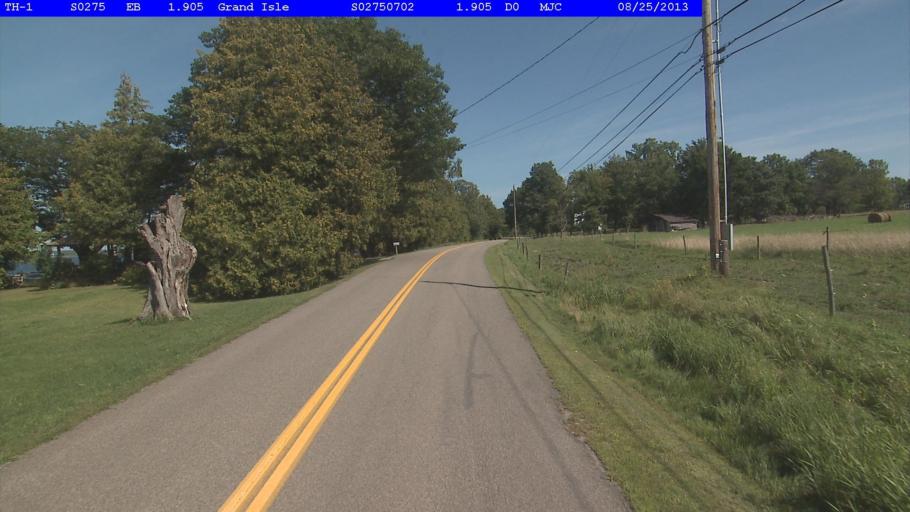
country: US
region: New York
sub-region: Clinton County
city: Cumberland Head
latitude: 44.7272
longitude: -73.3376
